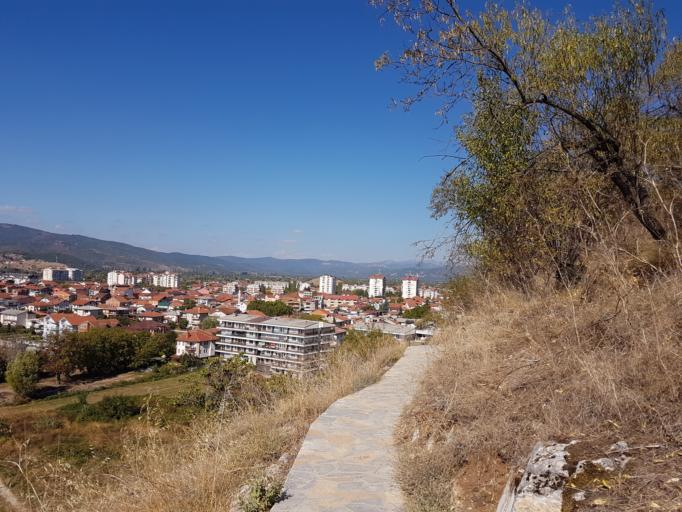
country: MK
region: Ohrid
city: Ohrid
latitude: 41.1153
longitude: 20.7886
